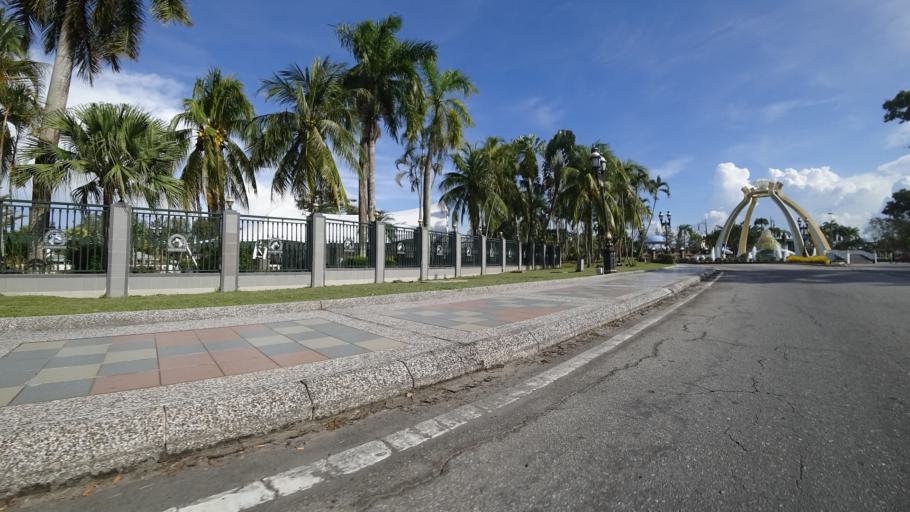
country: BN
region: Brunei and Muara
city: Bandar Seri Begawan
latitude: 4.9374
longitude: 114.8346
